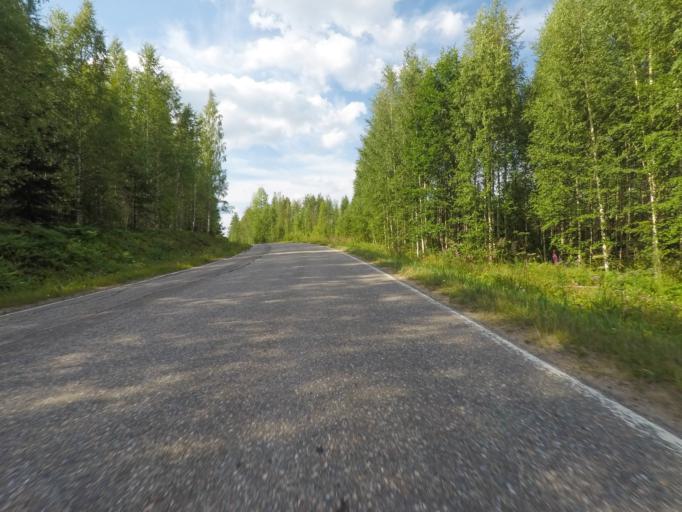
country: FI
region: Southern Savonia
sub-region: Mikkeli
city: Puumala
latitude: 61.6902
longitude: 28.2186
